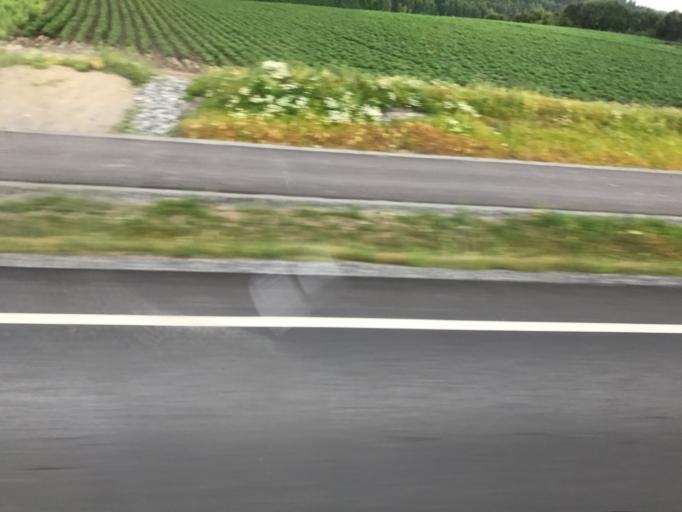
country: NO
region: Hedmark
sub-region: Stange
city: Stange
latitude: 60.6345
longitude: 11.0780
